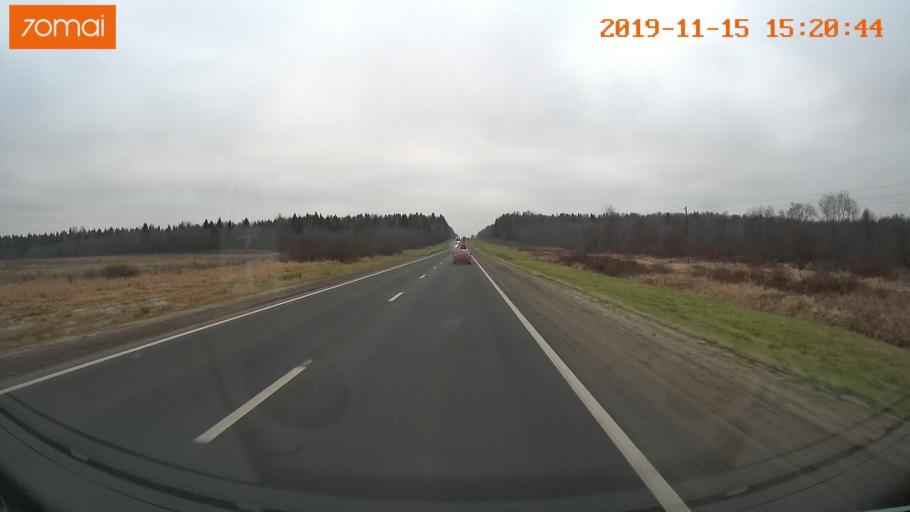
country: RU
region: Jaroslavl
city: Danilov
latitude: 58.2203
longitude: 40.1570
